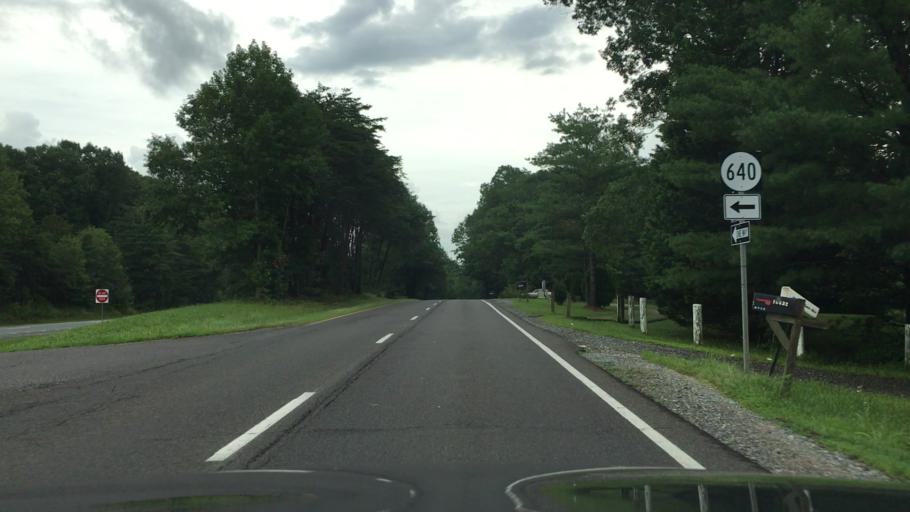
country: US
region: Virginia
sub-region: Spotsylvania County
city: Spotsylvania
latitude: 38.3201
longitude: -77.6968
